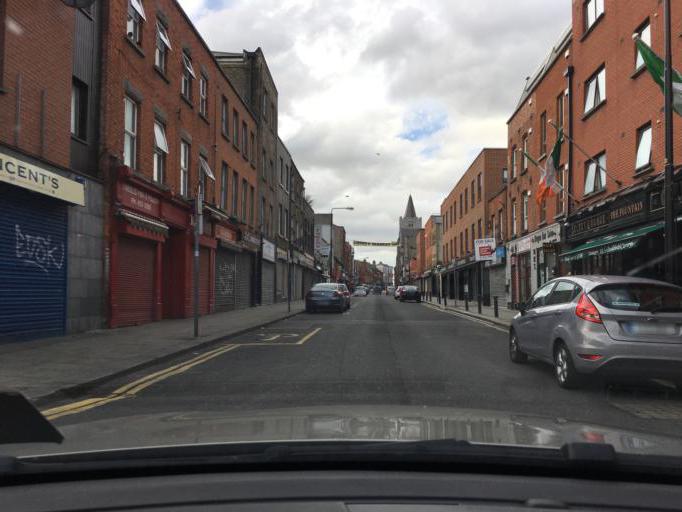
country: IE
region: Leinster
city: Rialto
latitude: 53.3405
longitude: -6.2782
